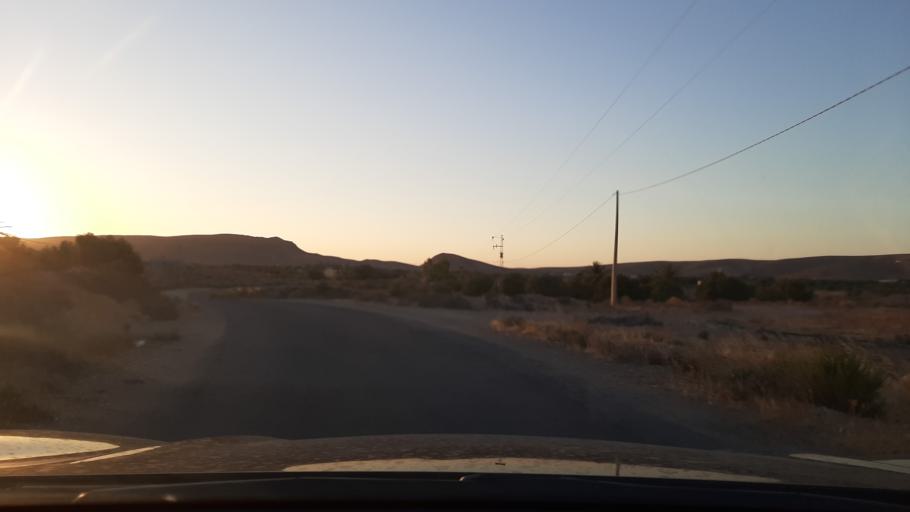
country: TN
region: Qabis
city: Matmata
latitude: 33.5613
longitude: 10.1824
